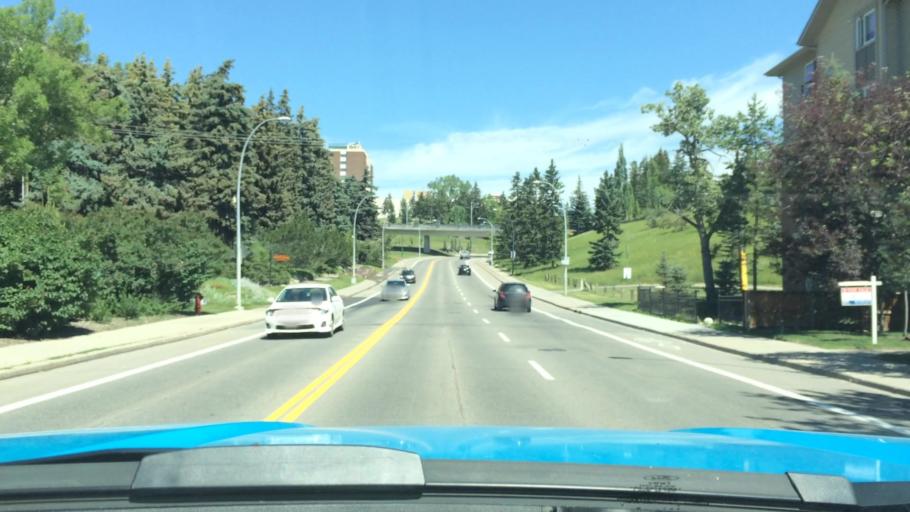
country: CA
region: Alberta
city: Calgary
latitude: 51.0591
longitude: -114.0860
